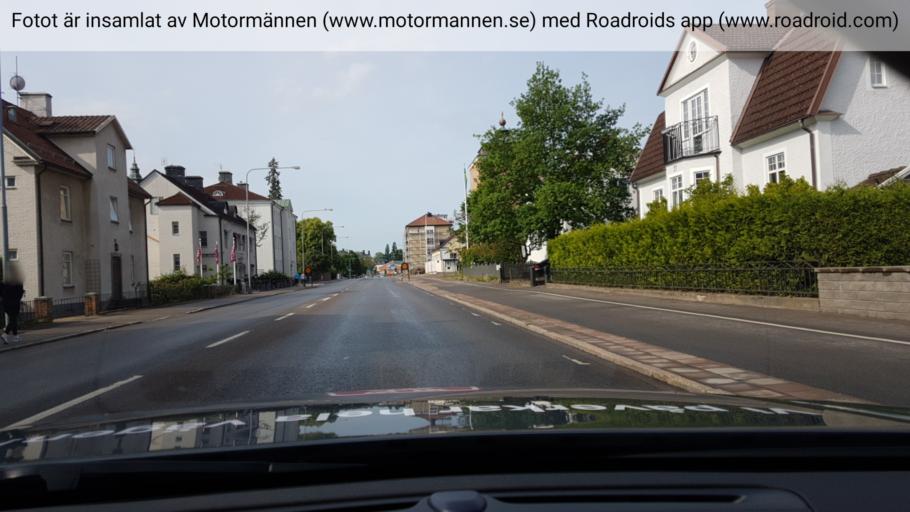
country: SE
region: OEstergoetland
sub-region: Motala Kommun
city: Motala
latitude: 58.5399
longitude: 15.0485
